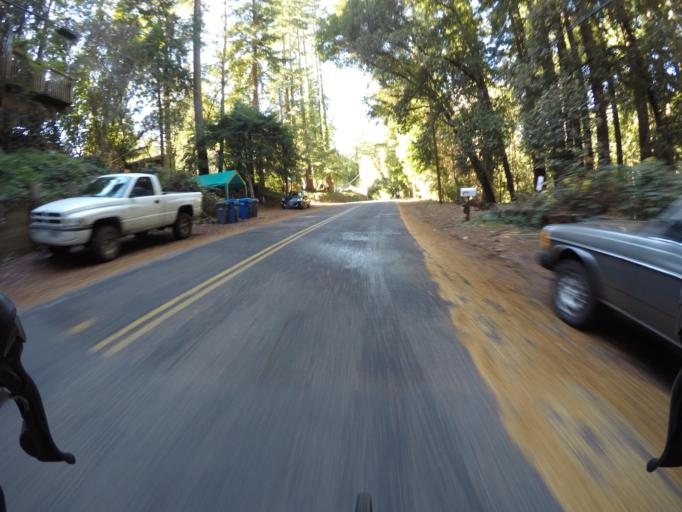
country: US
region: California
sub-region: Santa Cruz County
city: Mount Hermon
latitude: 37.0524
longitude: -122.0537
